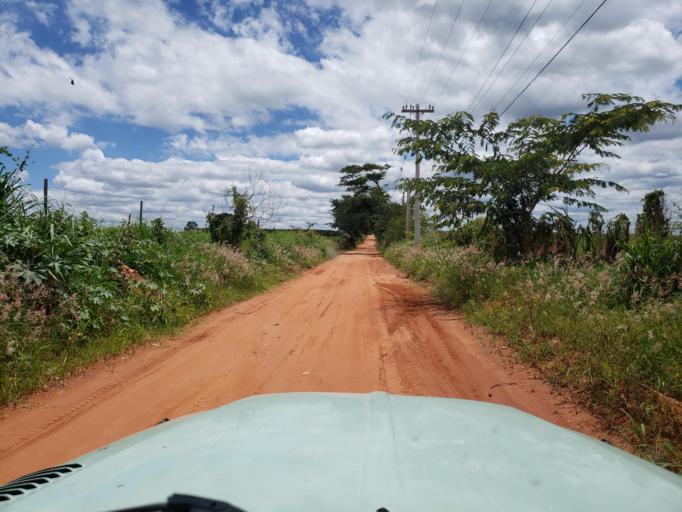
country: BR
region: Sao Paulo
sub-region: Aguai
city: Aguai
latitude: -22.1998
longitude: -46.9576
